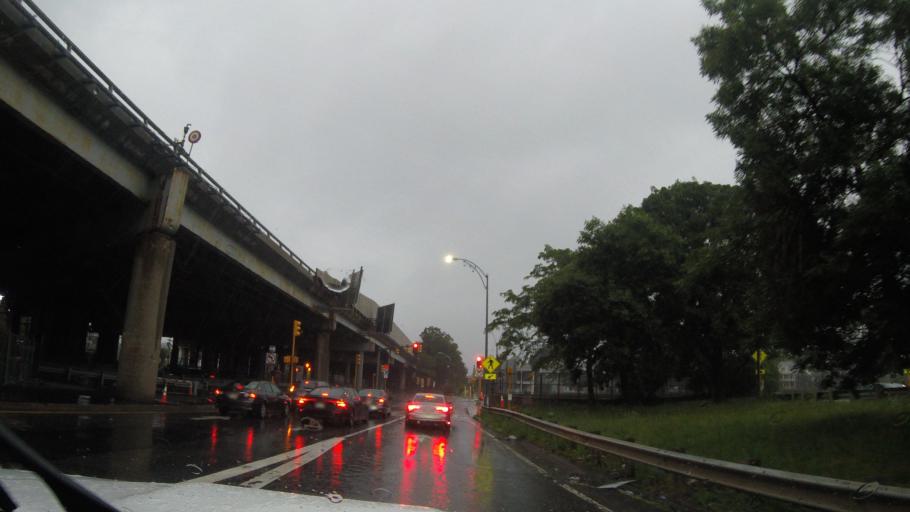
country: US
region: Massachusetts
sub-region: Middlesex County
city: Somerville
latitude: 42.3938
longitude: -71.0852
